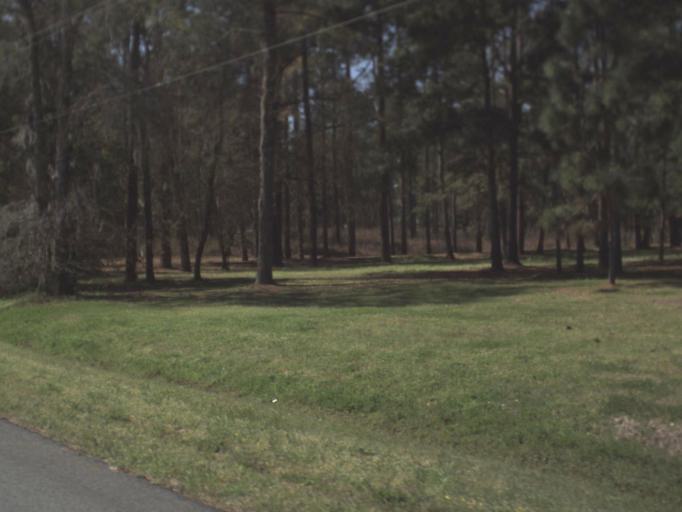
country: US
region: Florida
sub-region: Jefferson County
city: Monticello
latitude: 30.4089
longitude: -84.0209
